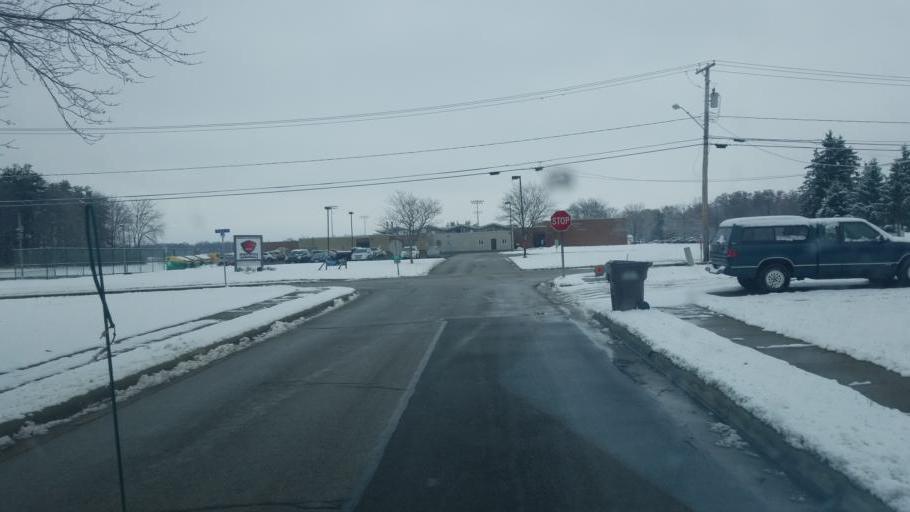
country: US
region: Ohio
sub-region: Geauga County
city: Middlefield
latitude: 41.4659
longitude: -81.0699
